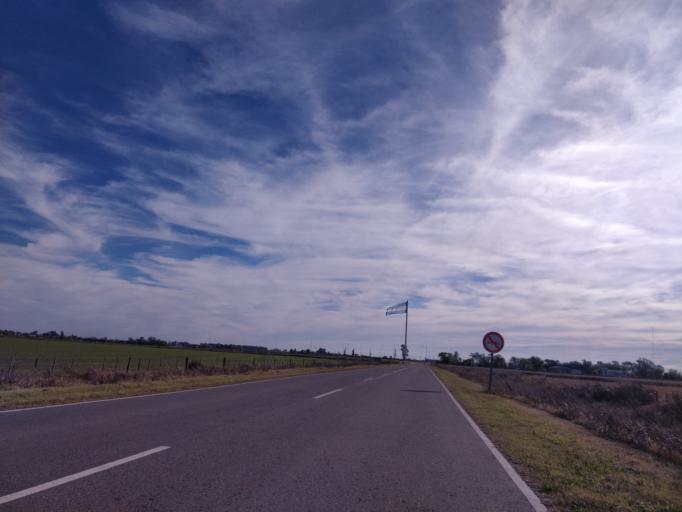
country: AR
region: Cordoba
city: Leones
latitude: -32.6429
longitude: -62.2864
